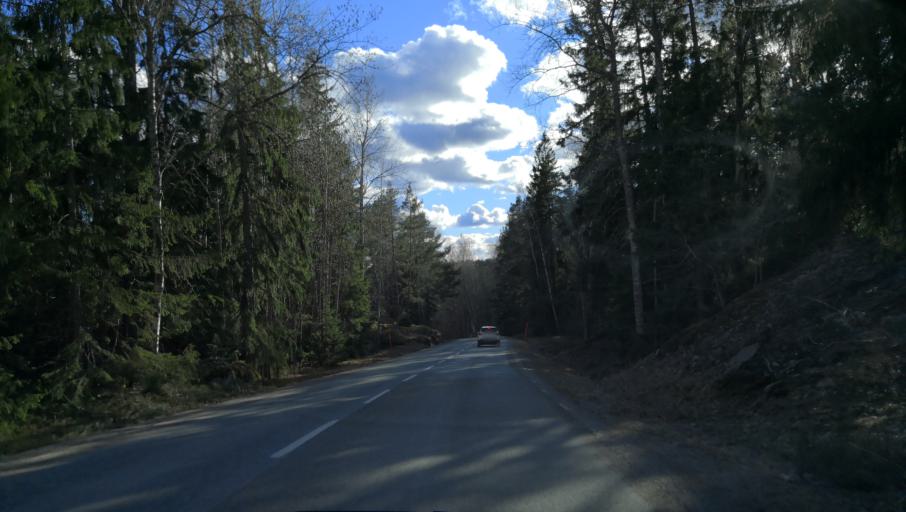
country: SE
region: Stockholm
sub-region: Varmdo Kommun
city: Mortnas
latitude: 59.2806
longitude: 18.4508
